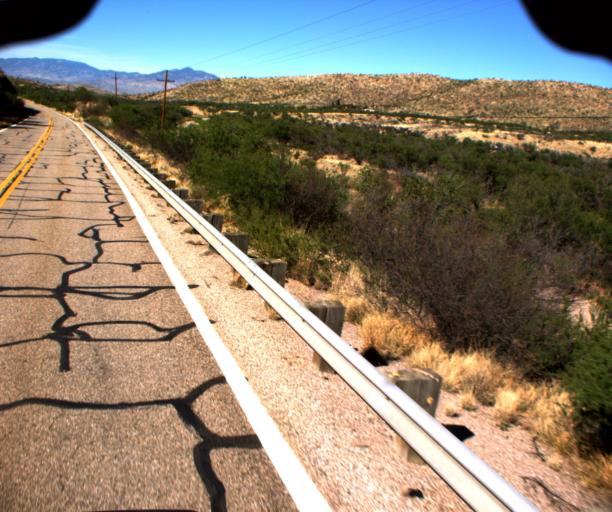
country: US
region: Arizona
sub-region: Pima County
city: Corona de Tucson
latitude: 31.8933
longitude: -110.6666
